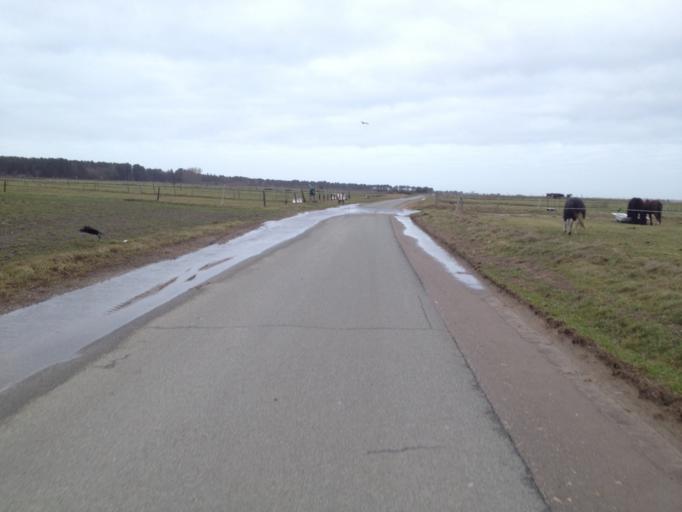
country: DE
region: Schleswig-Holstein
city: Nebel
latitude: 54.6589
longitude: 8.3496
